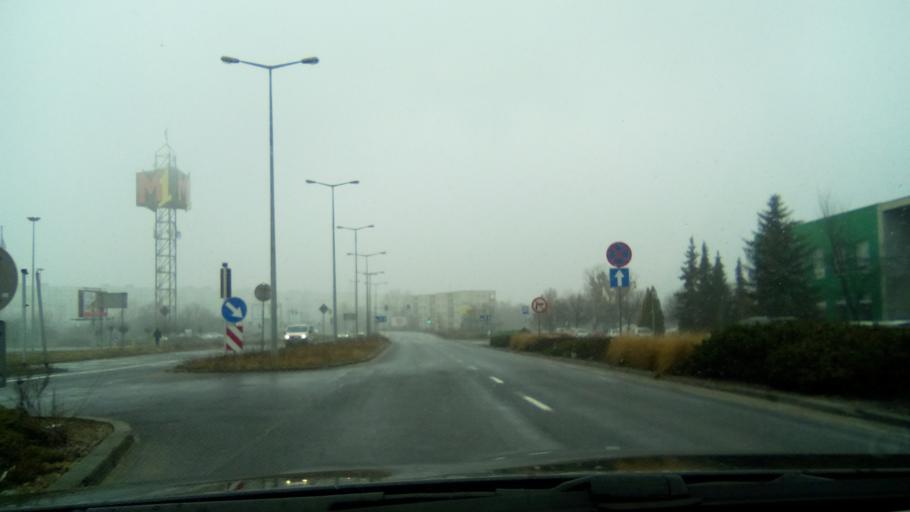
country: PL
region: Greater Poland Voivodeship
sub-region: Poznan
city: Poznan
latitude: 52.3845
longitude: 16.9969
